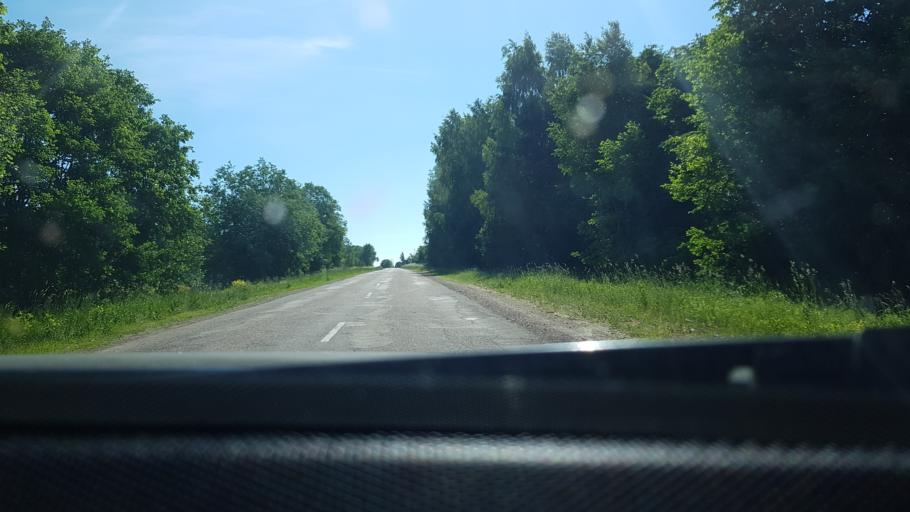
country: LV
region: Kraslavas Rajons
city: Kraslava
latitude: 55.8626
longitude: 27.0237
